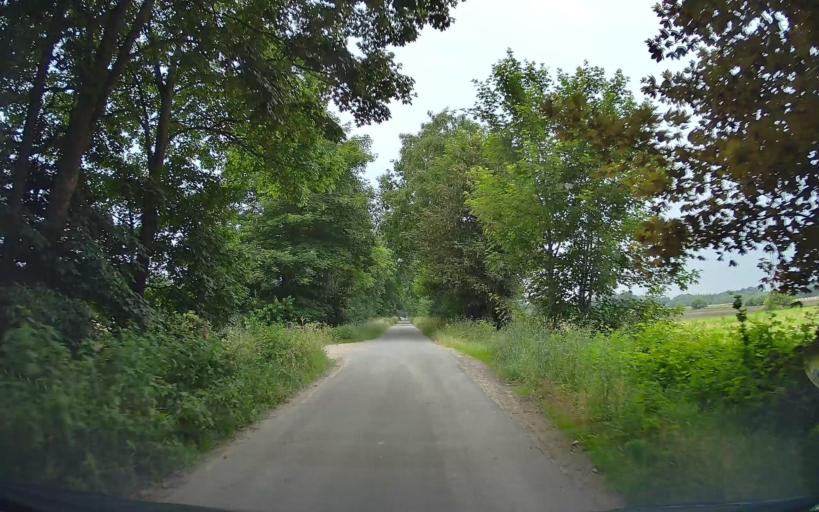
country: DE
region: Lower Saxony
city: Friesoythe
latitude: 53.0108
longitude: 7.8836
